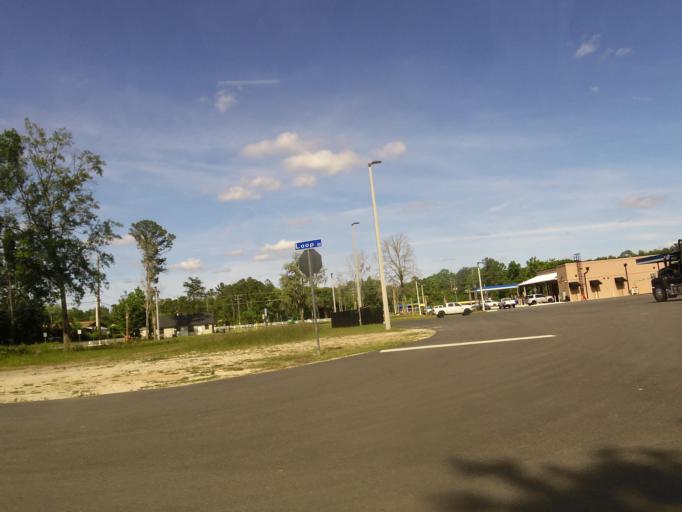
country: US
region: Florida
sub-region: Nassau County
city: Callahan
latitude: 30.5703
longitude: -81.8374
